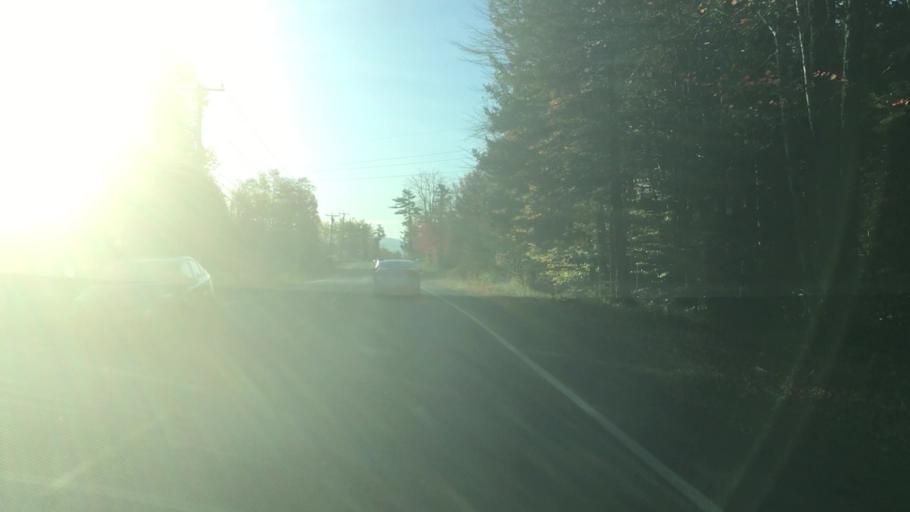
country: US
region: Maine
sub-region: Hancock County
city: Ellsworth
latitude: 44.5111
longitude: -68.3923
